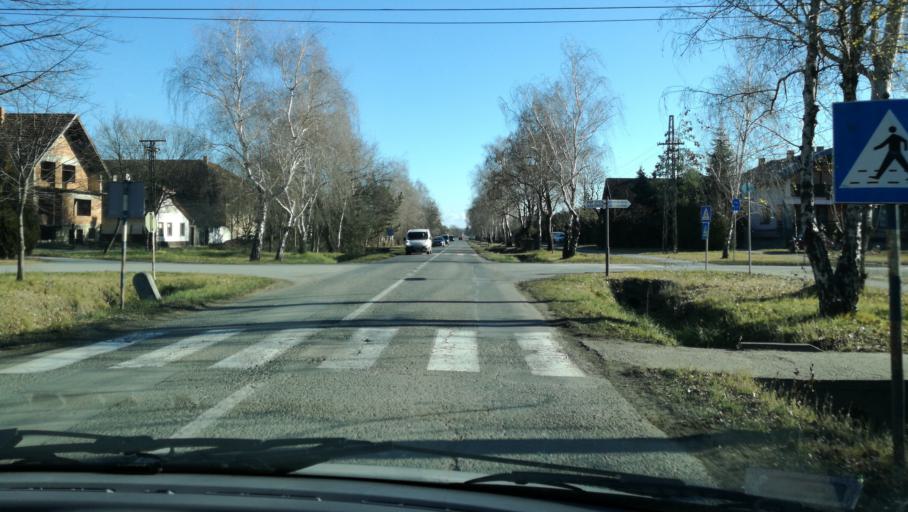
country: HU
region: Csongrad
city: Roszke
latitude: 46.1515
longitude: 19.9678
